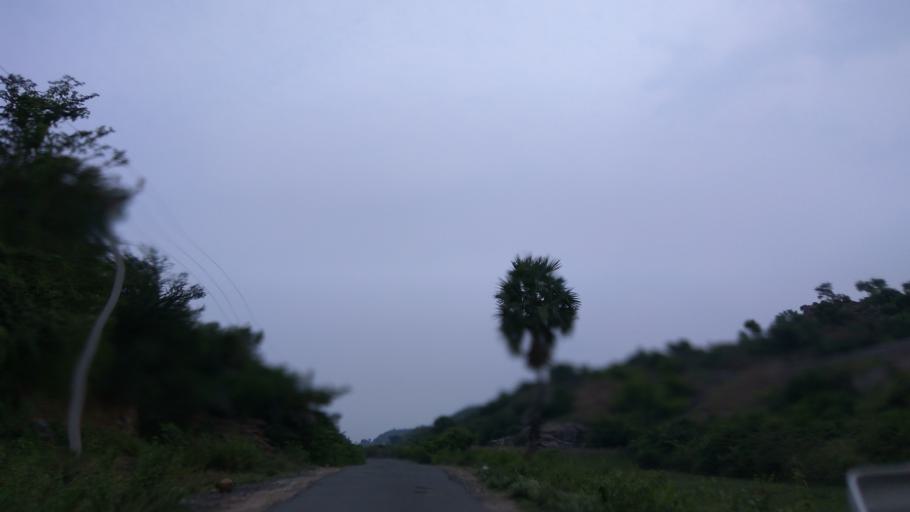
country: IN
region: Tamil Nadu
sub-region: Dharmapuri
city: Dharmapuri
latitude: 12.0200
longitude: 78.1206
